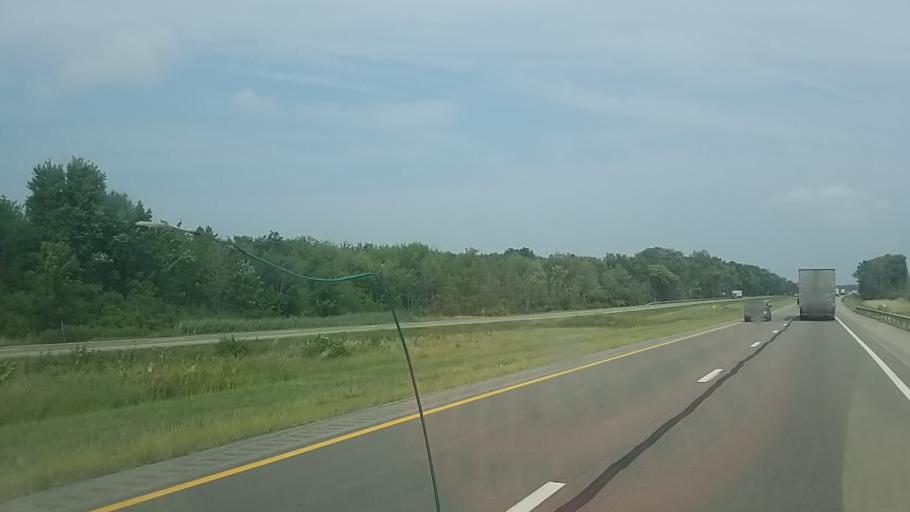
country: US
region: New York
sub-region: Erie County
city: Hamburg
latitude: 42.7349
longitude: -78.8581
